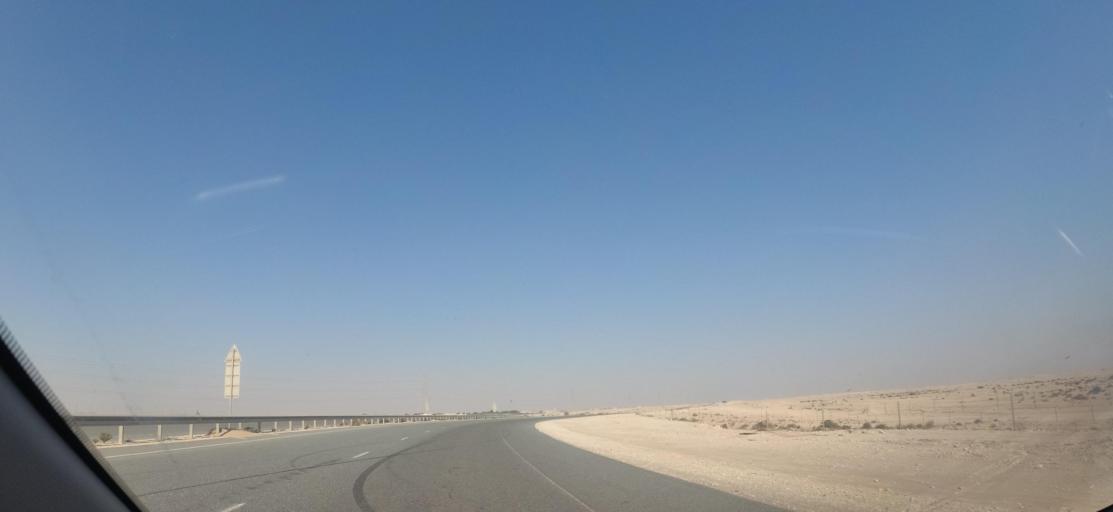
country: QA
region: Baladiyat ar Rayyan
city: Dukhan
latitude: 25.4713
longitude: 50.9338
